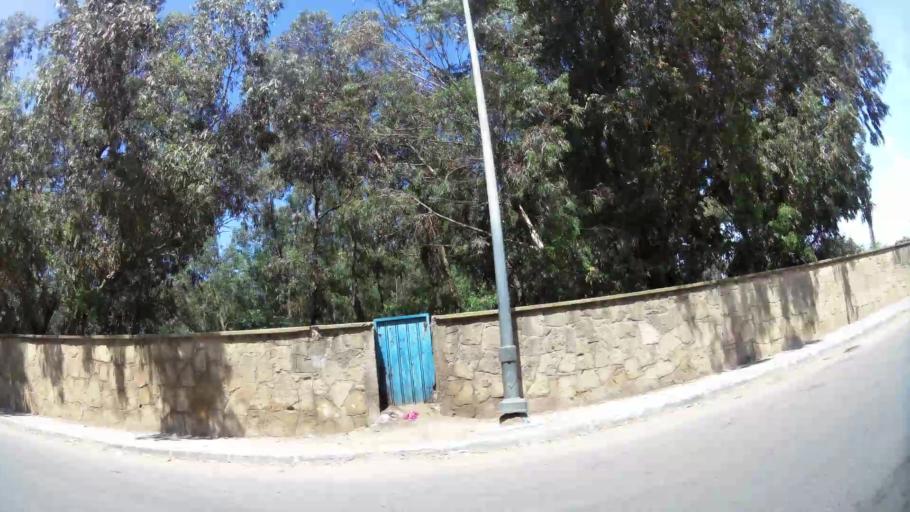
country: MA
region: Gharb-Chrarda-Beni Hssen
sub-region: Kenitra Province
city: Kenitra
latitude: 34.2317
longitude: -6.5344
